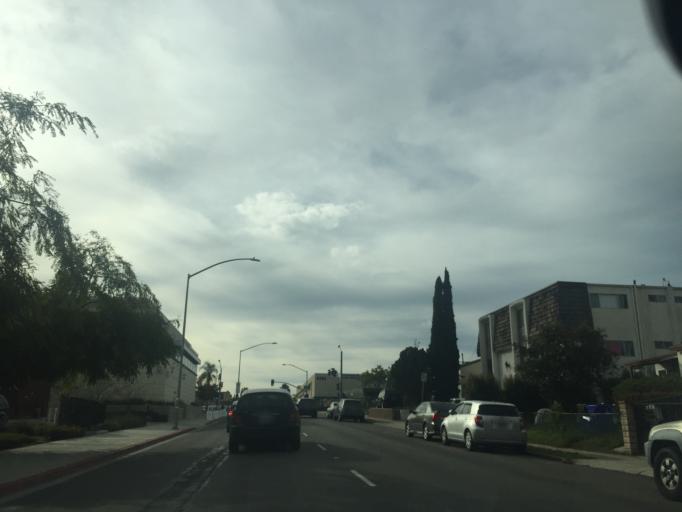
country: US
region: California
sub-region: San Diego County
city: San Diego
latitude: 32.7562
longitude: -117.1019
